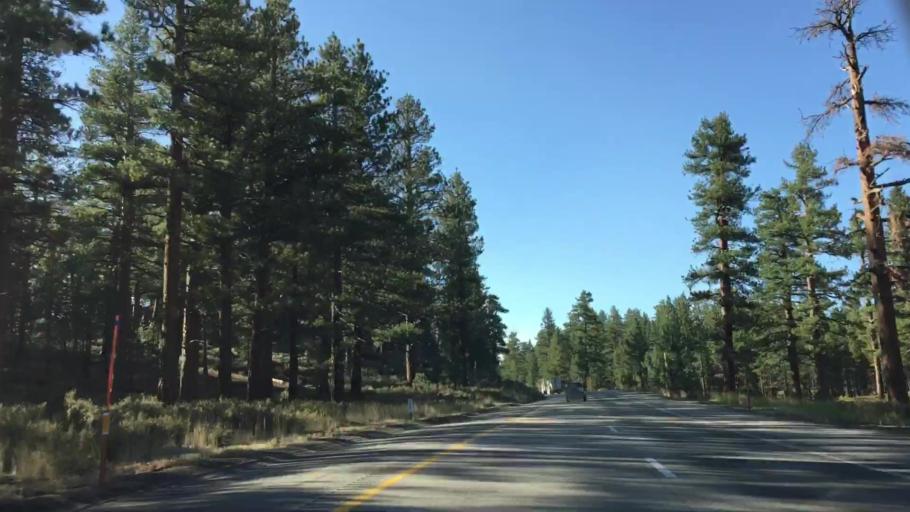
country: US
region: California
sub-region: Mono County
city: Mammoth Lakes
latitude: 37.6663
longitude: -118.9327
